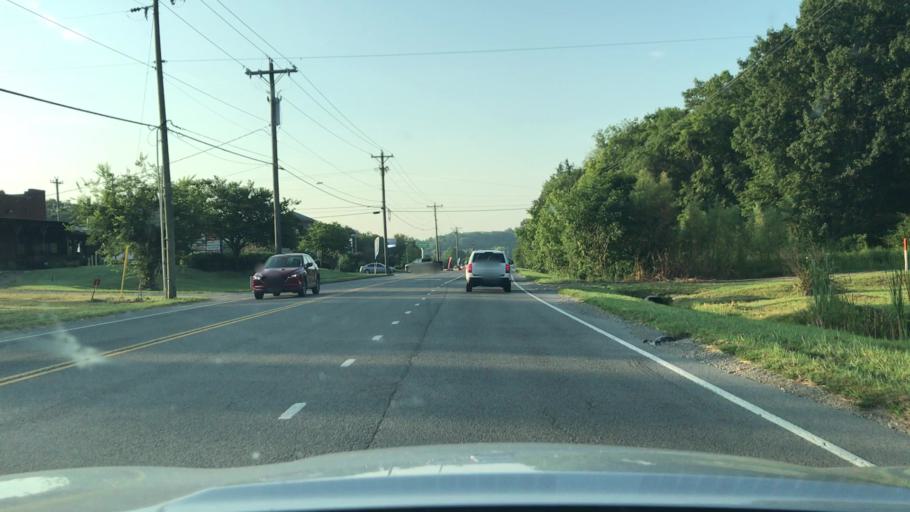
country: US
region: Tennessee
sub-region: Williamson County
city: Brentwood Estates
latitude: 36.0162
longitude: -86.7063
